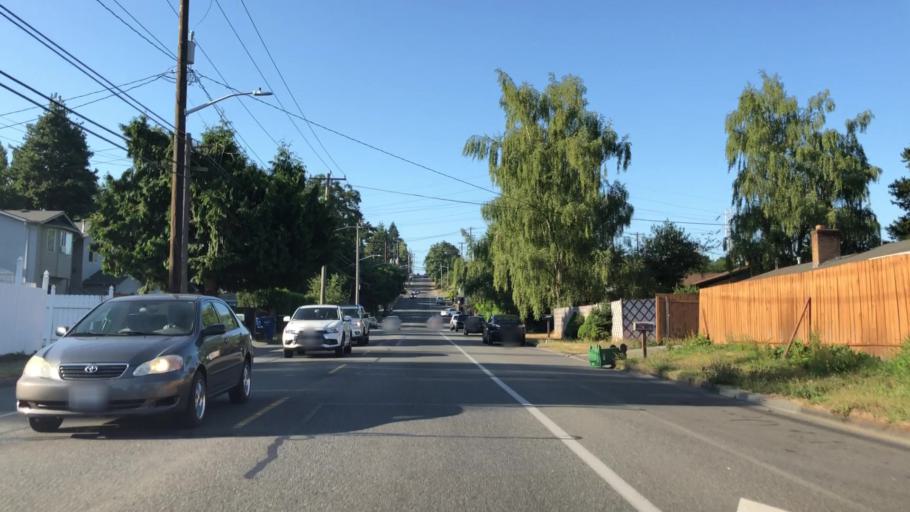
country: US
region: Washington
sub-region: King County
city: Bryn Mawr-Skyway
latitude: 47.5087
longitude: -122.2701
